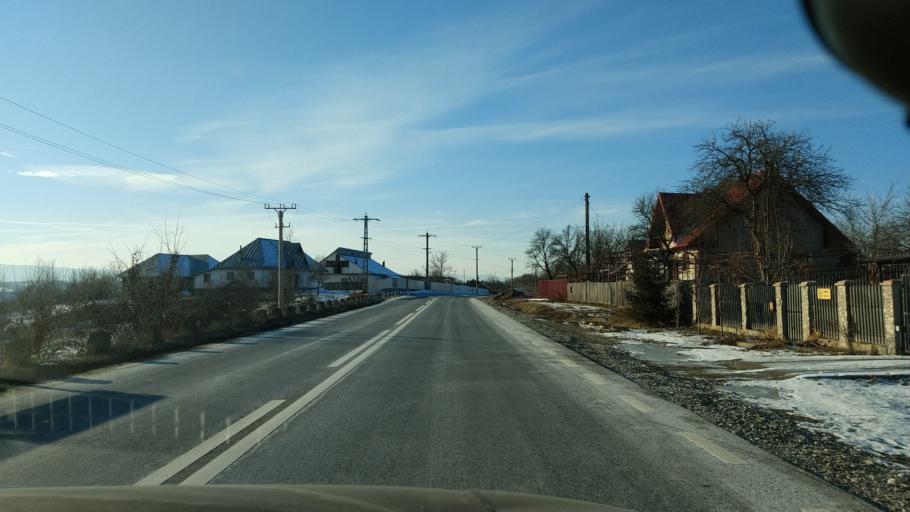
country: RO
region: Bacau
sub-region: Comuna Luizi-Calugara
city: Luizi-Calugara
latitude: 46.4920
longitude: 26.7858
